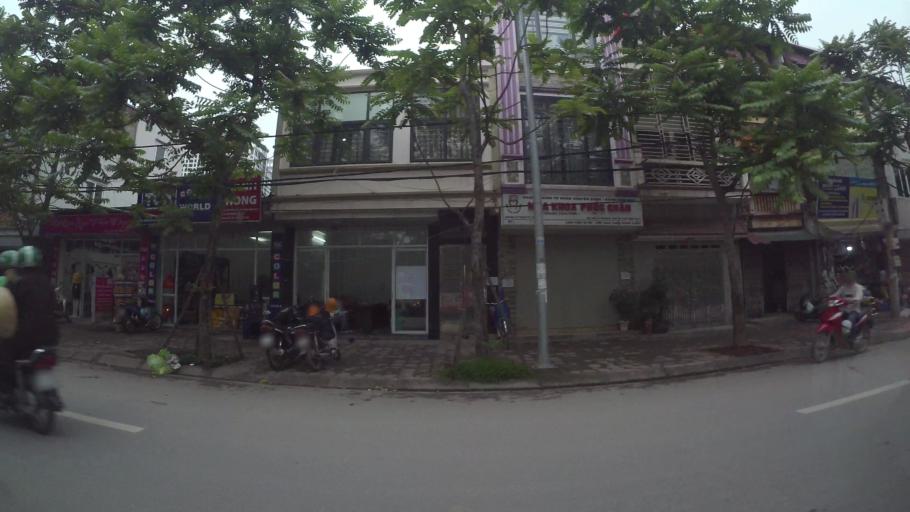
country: VN
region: Ha Noi
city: Hai BaTrung
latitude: 20.9939
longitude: 105.8739
